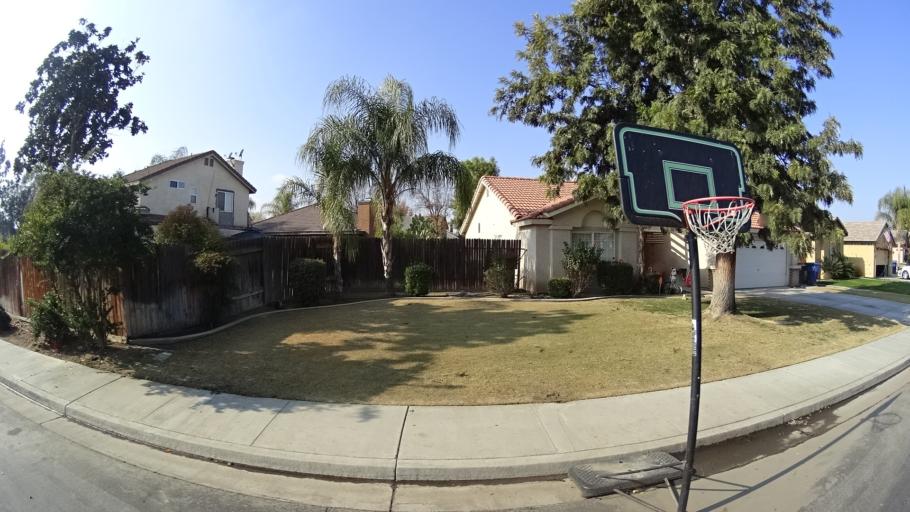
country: US
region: California
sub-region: Kern County
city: Greenacres
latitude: 35.3056
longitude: -119.0806
